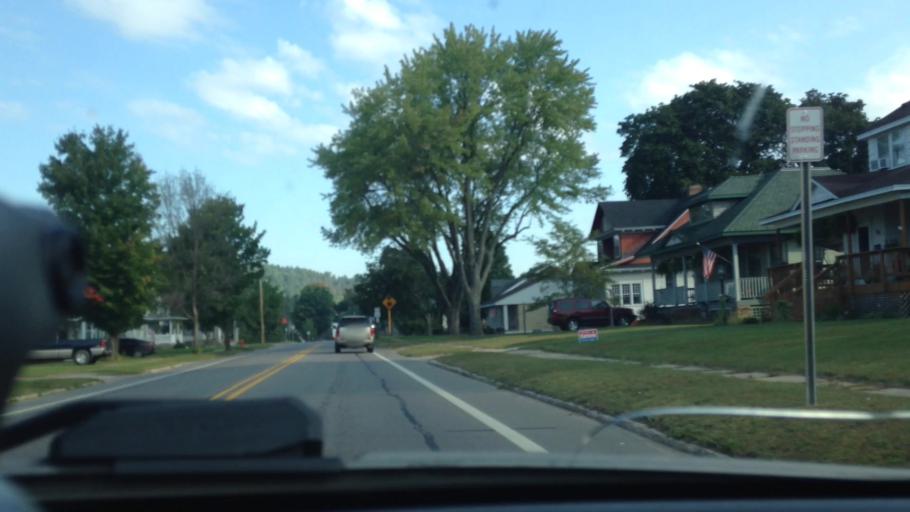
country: US
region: Michigan
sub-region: Dickinson County
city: Norway
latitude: 45.7850
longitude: -87.9098
